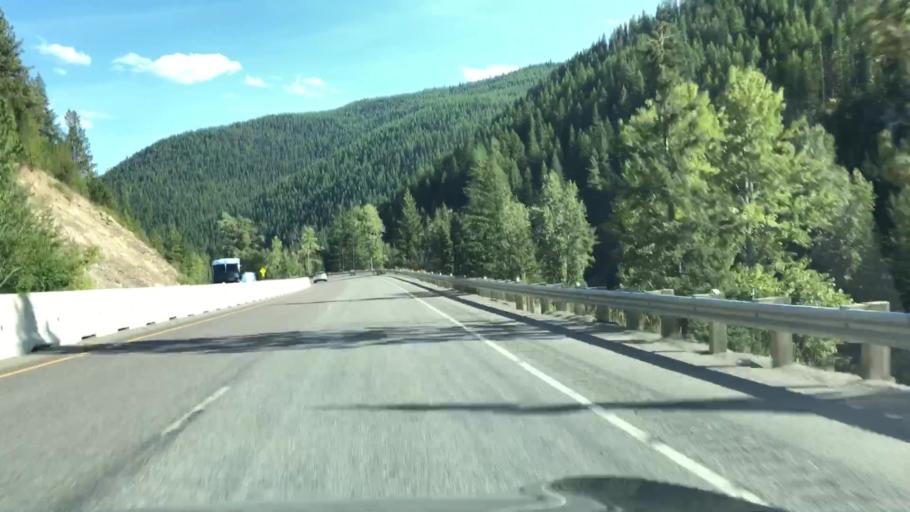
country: US
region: Montana
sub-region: Sanders County
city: Thompson Falls
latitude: 47.4002
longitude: -115.4618
